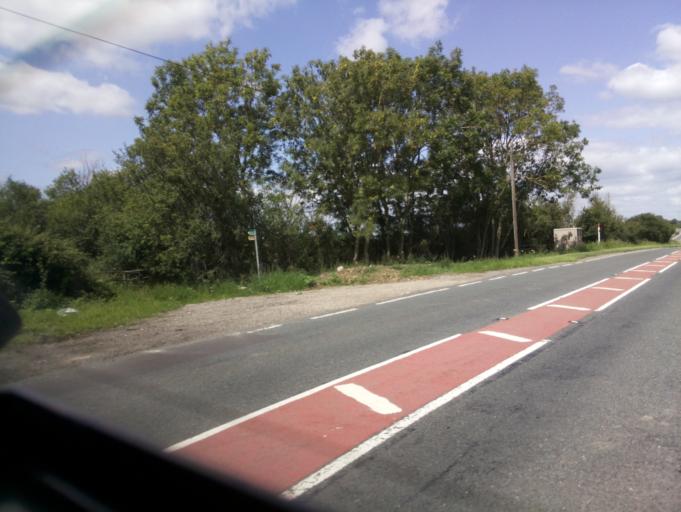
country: GB
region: England
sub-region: Buckinghamshire
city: Aylesbury
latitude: 51.8436
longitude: -0.8212
